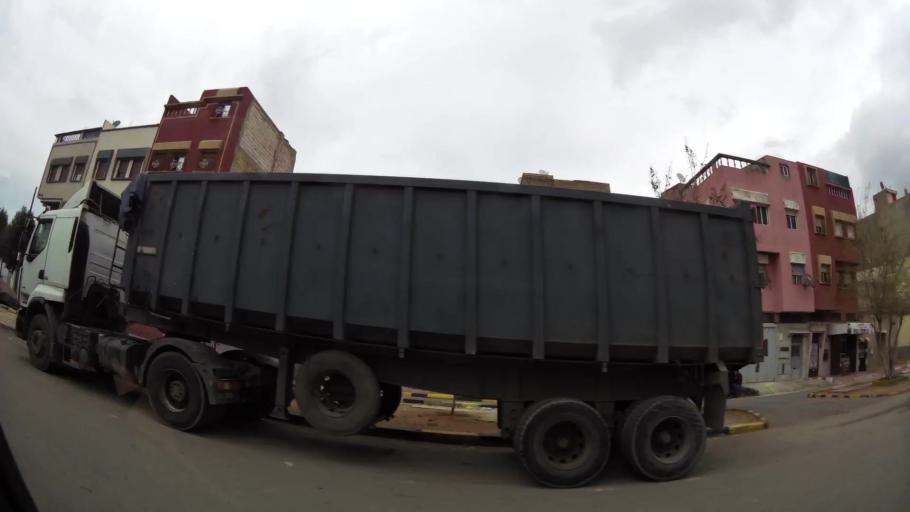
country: MA
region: Grand Casablanca
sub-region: Casablanca
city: Casablanca
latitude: 33.5563
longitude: -7.5535
